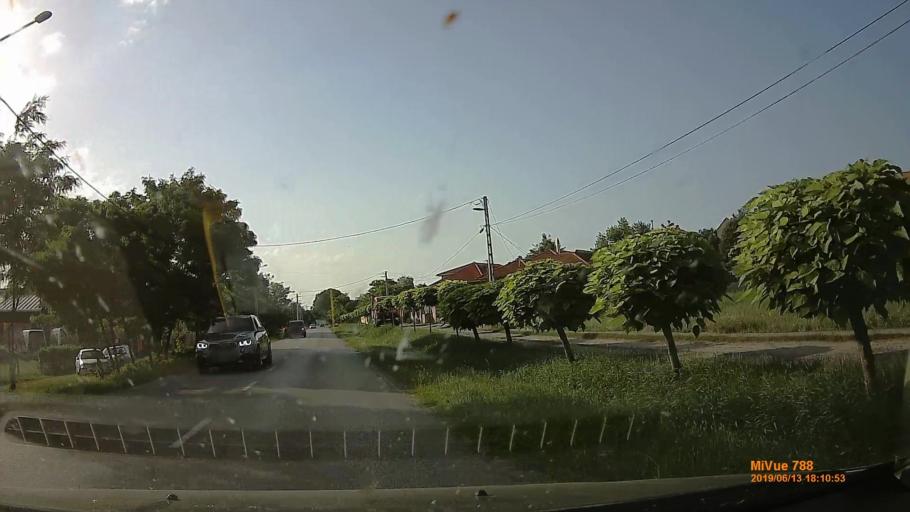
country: HU
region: Pest
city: Ecser
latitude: 47.4503
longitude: 19.3065
